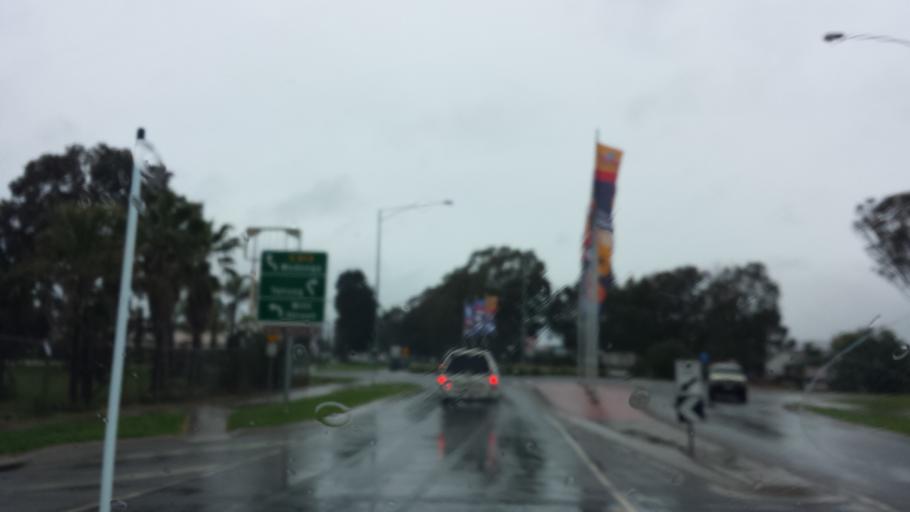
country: AU
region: Victoria
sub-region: Benalla
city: Benalla
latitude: -36.5488
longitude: 145.9966
